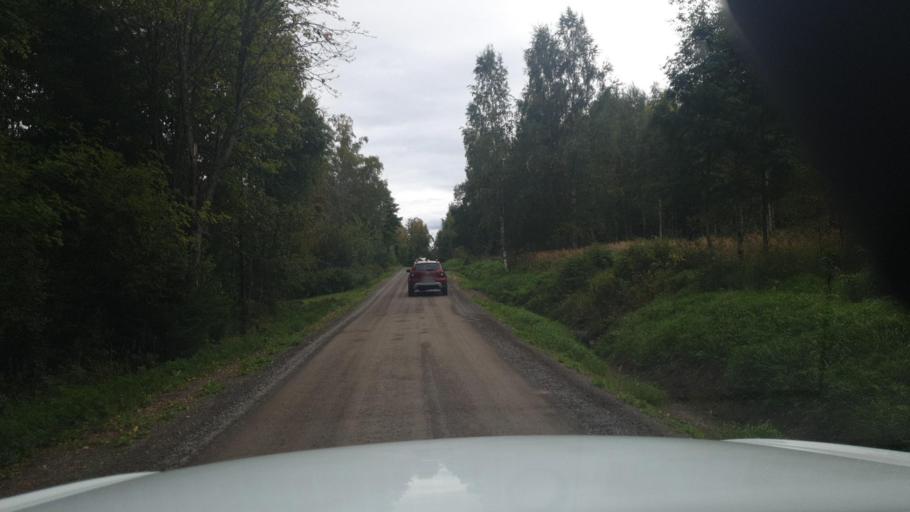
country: SE
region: Vaermland
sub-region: Torsby Kommun
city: Torsby
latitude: 59.9615
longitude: 12.8845
